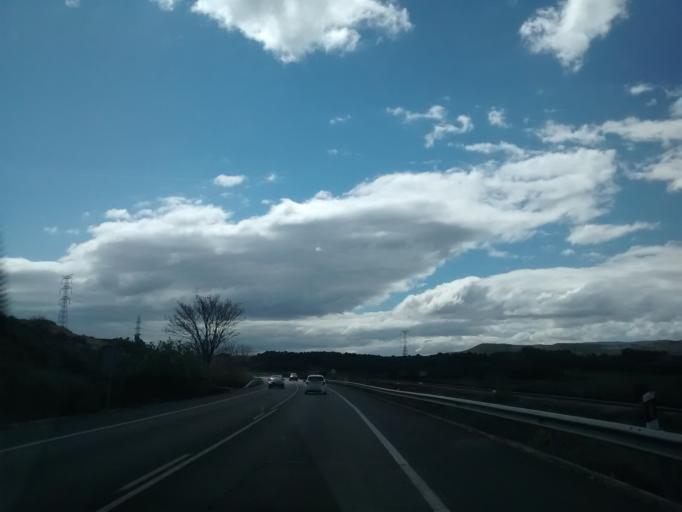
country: ES
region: La Rioja
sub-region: Provincia de La Rioja
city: Arrubal
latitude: 42.4045
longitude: -2.2499
